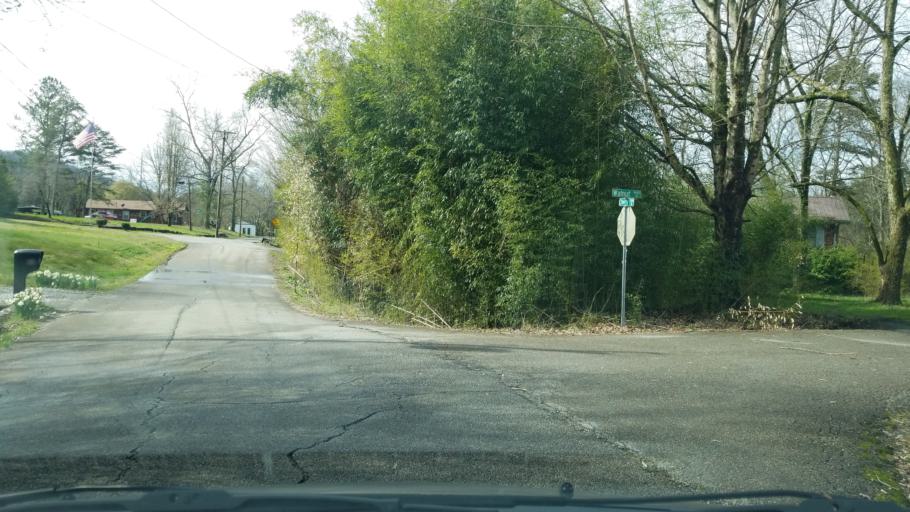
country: US
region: Tennessee
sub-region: Hamilton County
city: Collegedale
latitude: 35.0696
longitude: -85.0592
